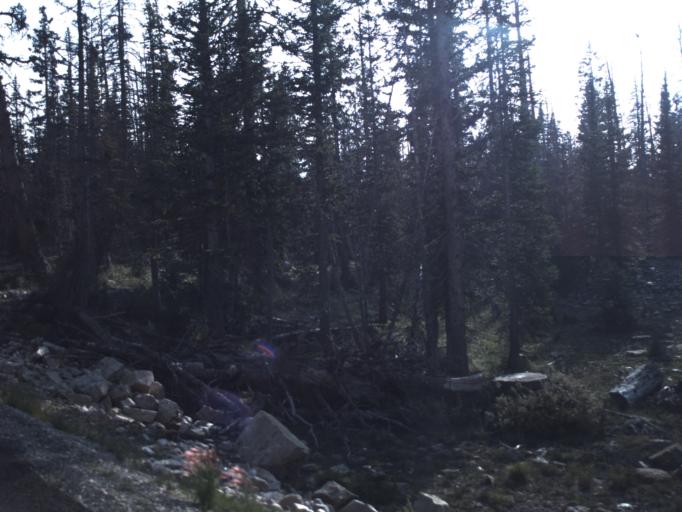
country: US
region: Utah
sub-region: Summit County
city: Kamas
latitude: 40.7252
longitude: -110.8646
